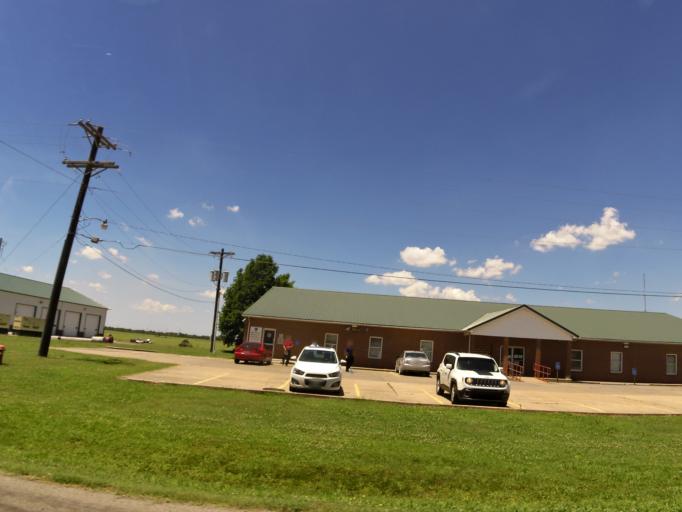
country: US
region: Missouri
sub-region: New Madrid County
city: New Madrid
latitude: 36.5831
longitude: -89.5522
